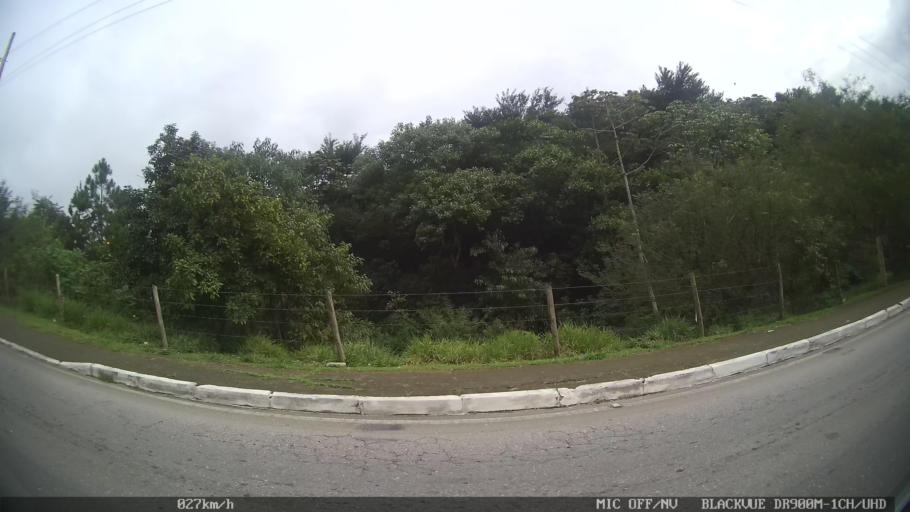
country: BR
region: Santa Catarina
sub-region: Sao Jose
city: Campinas
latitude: -27.5531
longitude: -48.6443
